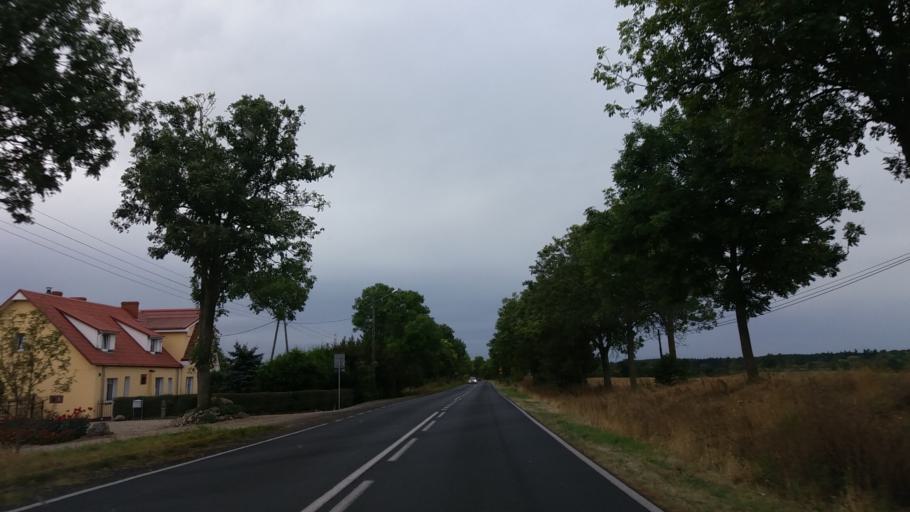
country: PL
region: West Pomeranian Voivodeship
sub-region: Powiat mysliborski
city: Barlinek
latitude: 52.9661
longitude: 15.1852
